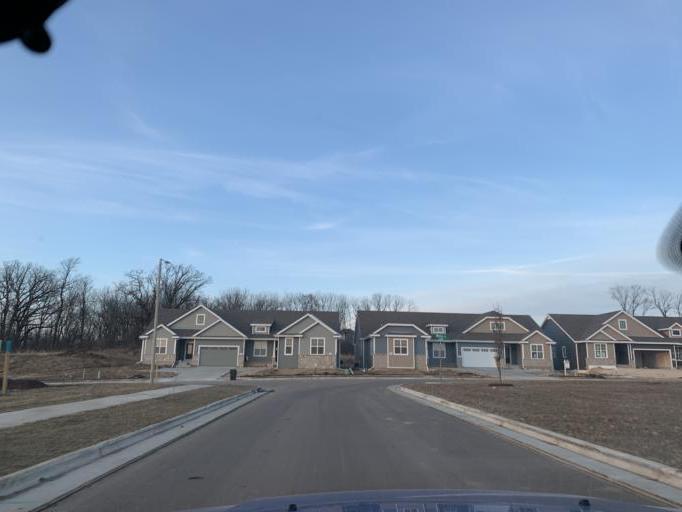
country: US
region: Wisconsin
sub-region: Dane County
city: Verona
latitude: 43.0520
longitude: -89.5650
